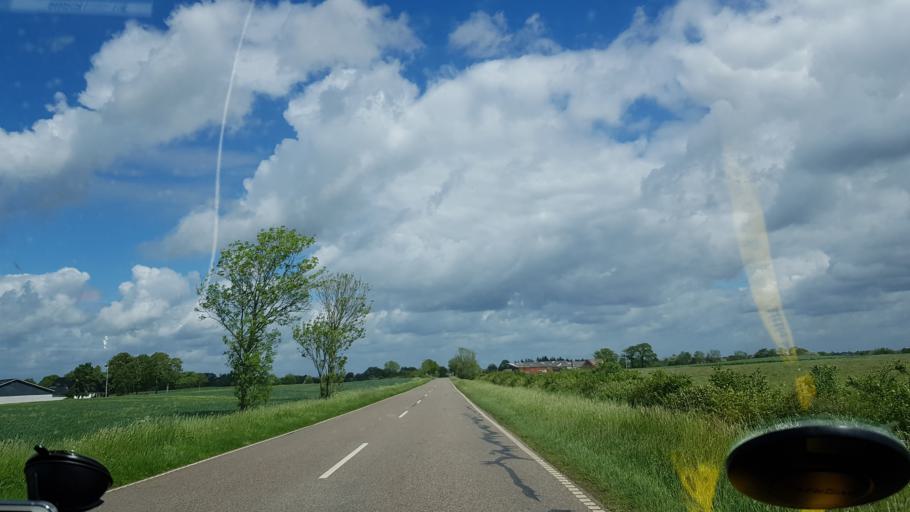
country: DK
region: South Denmark
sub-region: Kolding Kommune
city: Christiansfeld
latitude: 55.3358
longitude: 9.4550
